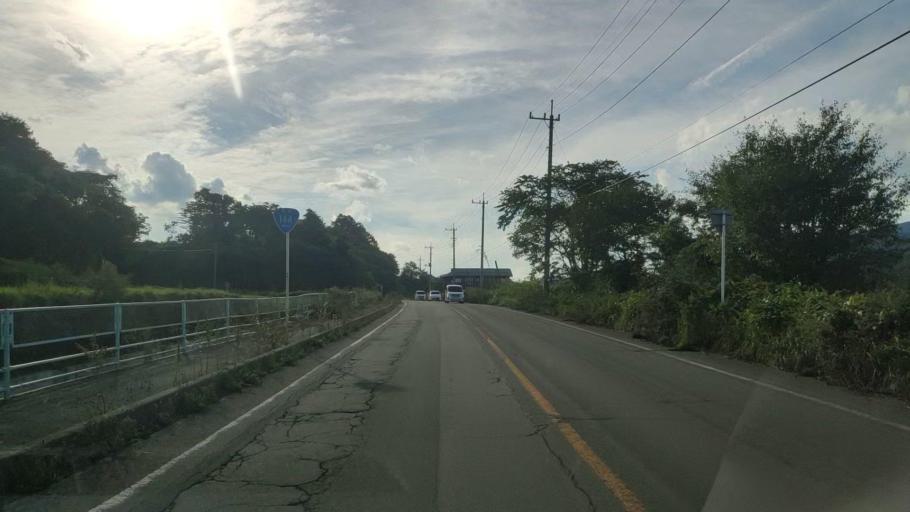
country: JP
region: Nagano
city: Komoro
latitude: 36.4849
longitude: 138.4596
